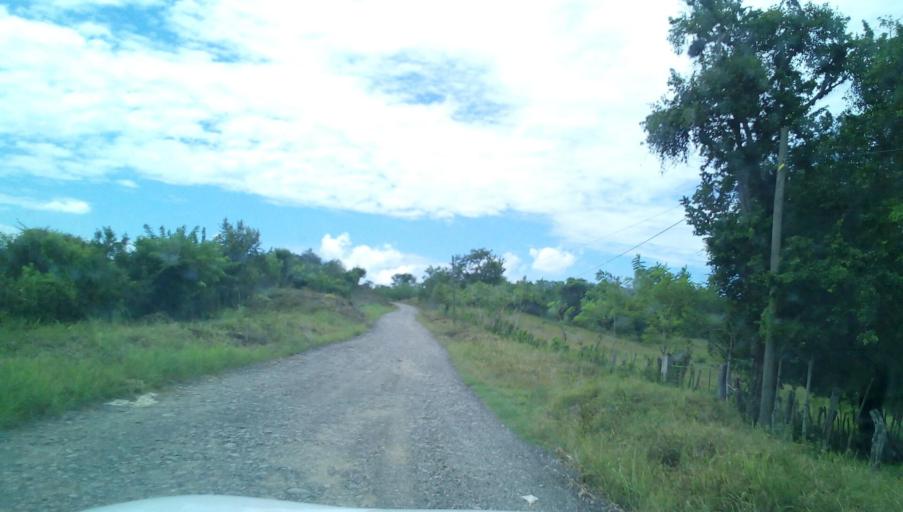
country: MX
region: Veracruz
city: Tepetzintla
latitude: 21.1541
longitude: -97.8536
